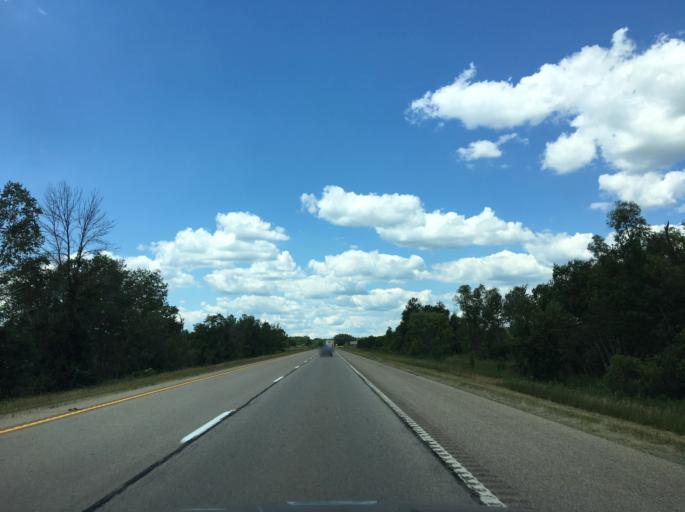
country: US
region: Michigan
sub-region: Clare County
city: Clare
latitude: 43.8819
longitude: -84.7902
